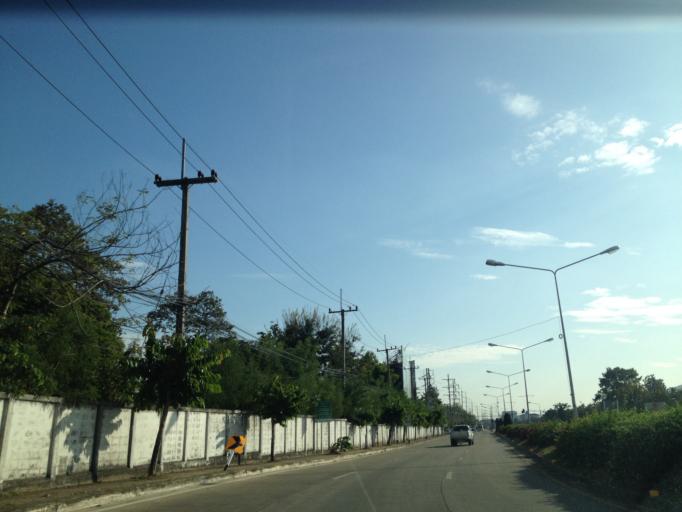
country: TH
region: Chiang Mai
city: Chiang Mai
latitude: 18.8415
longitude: 98.9654
